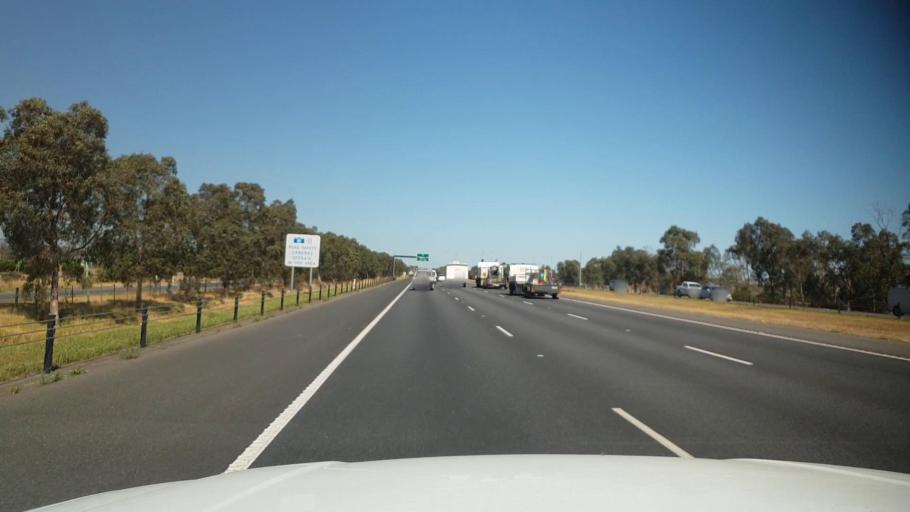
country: AU
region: Victoria
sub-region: Frankston
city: Sandhurst
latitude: -38.0547
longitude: 145.1850
